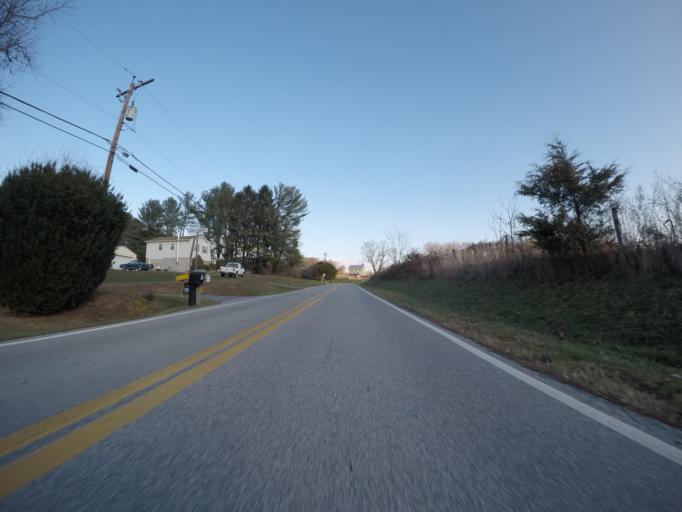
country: US
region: Maryland
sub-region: Carroll County
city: Hampstead
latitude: 39.5722
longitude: -76.9015
